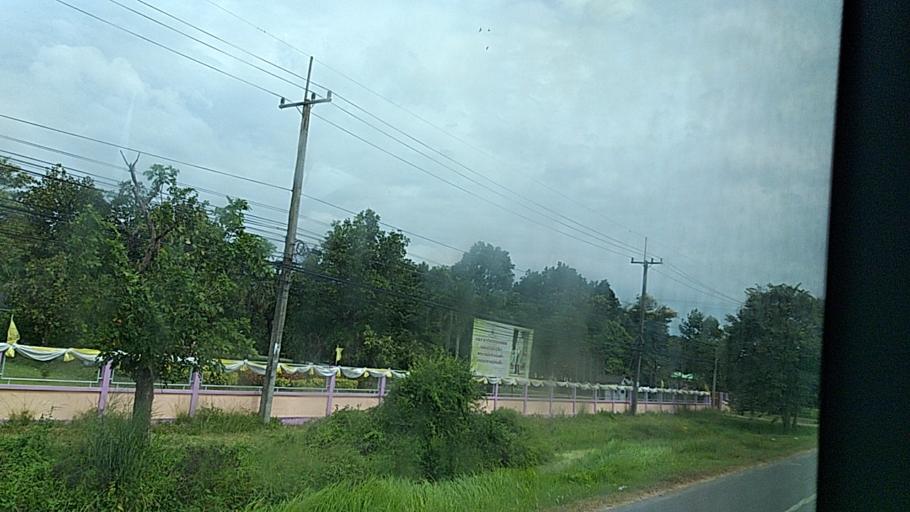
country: TH
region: Roi Et
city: Roi Et
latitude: 16.0701
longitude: 103.6028
